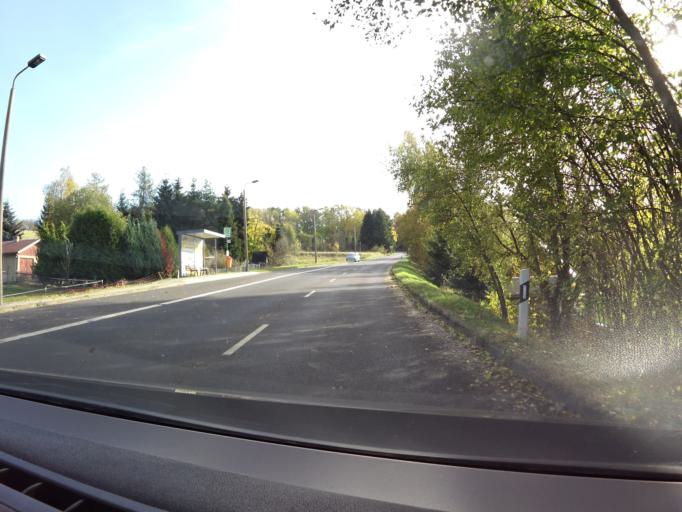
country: DE
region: Thuringia
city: Martinroda
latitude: 50.6982
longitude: 10.8920
